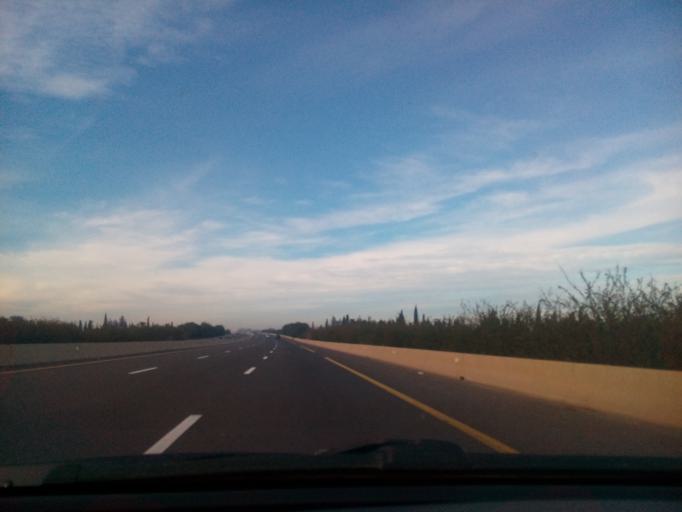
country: DZ
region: Mascara
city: Mascara
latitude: 35.6219
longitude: 0.0525
